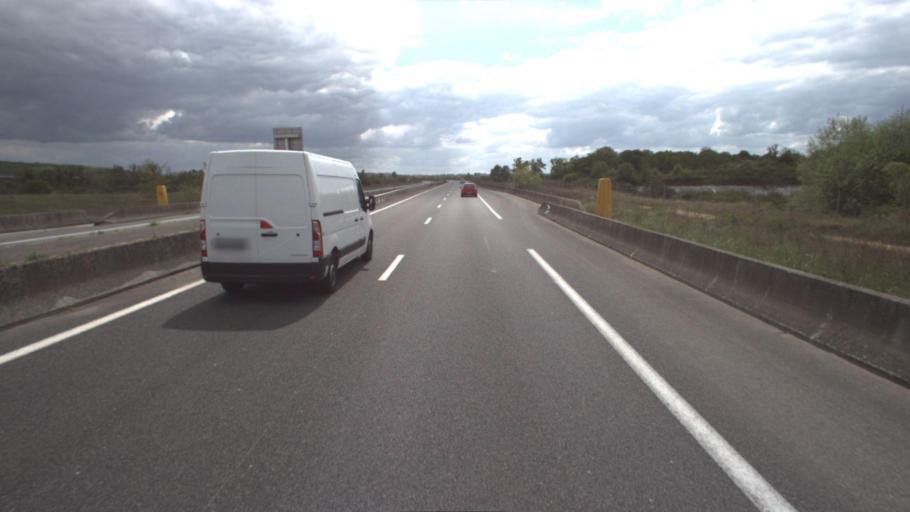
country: FR
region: Ile-de-France
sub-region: Departement de Seine-et-Marne
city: Mareuil-les-Meaux
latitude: 48.9281
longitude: 2.8452
